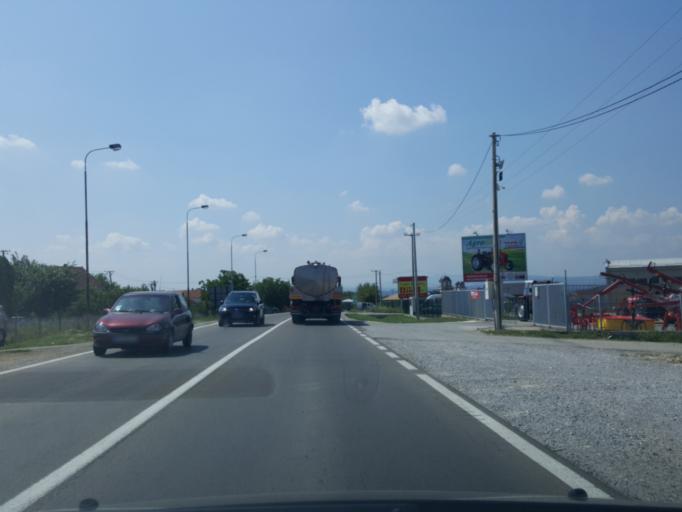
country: RS
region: Central Serbia
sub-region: Belgrade
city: Mladenovac
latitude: 44.4204
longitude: 20.6814
